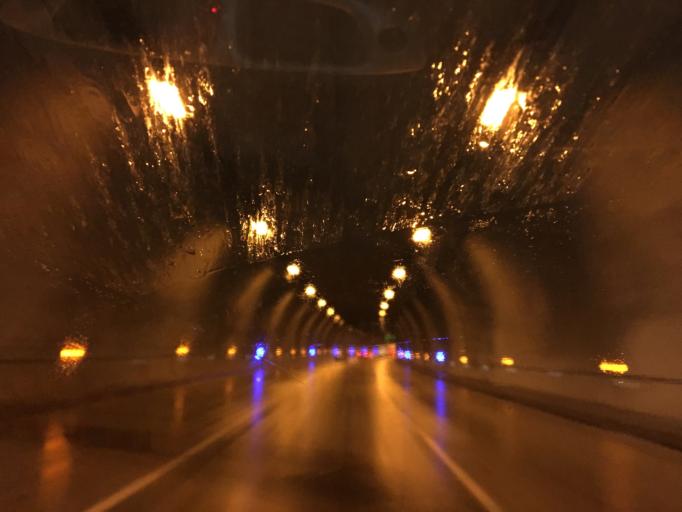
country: DZ
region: Boumerdes
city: Arbatache
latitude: 36.5863
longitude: 3.4631
